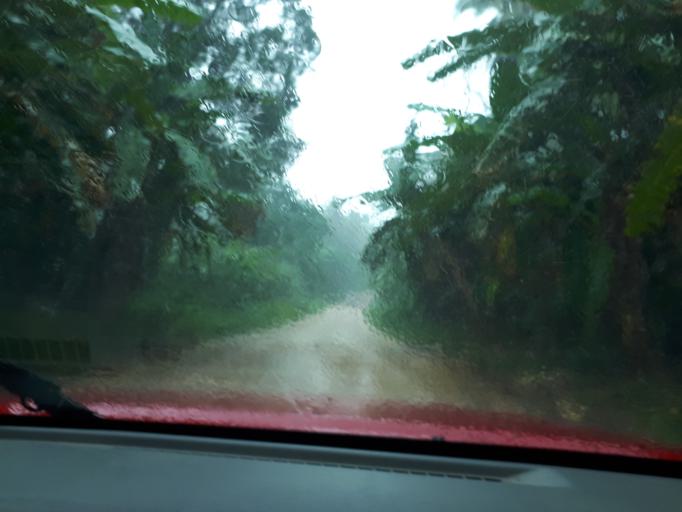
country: VU
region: Sanma
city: Luganville
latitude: -15.5582
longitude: 166.9948
